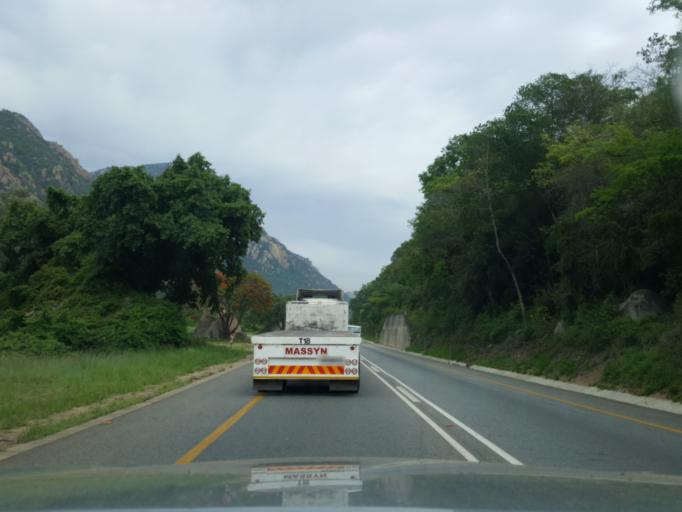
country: ZA
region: Mpumalanga
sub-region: Ehlanzeni District
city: Nelspruit
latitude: -25.5204
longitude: 31.2492
